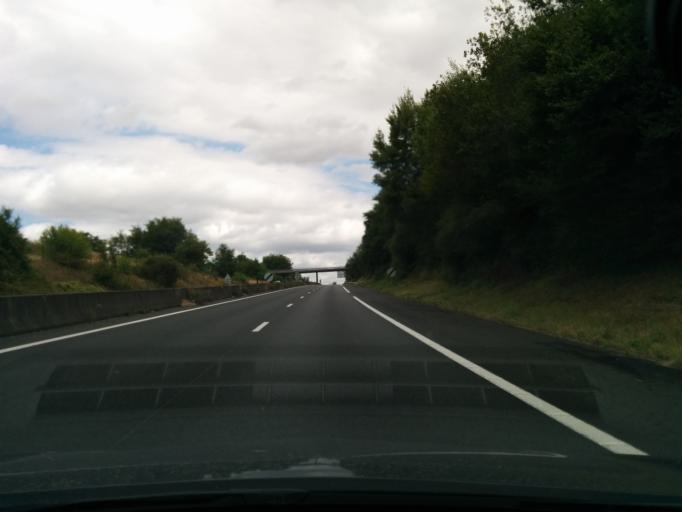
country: FR
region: Centre
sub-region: Departement de l'Indre
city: Saint-Marcel
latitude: 46.6041
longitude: 1.5004
